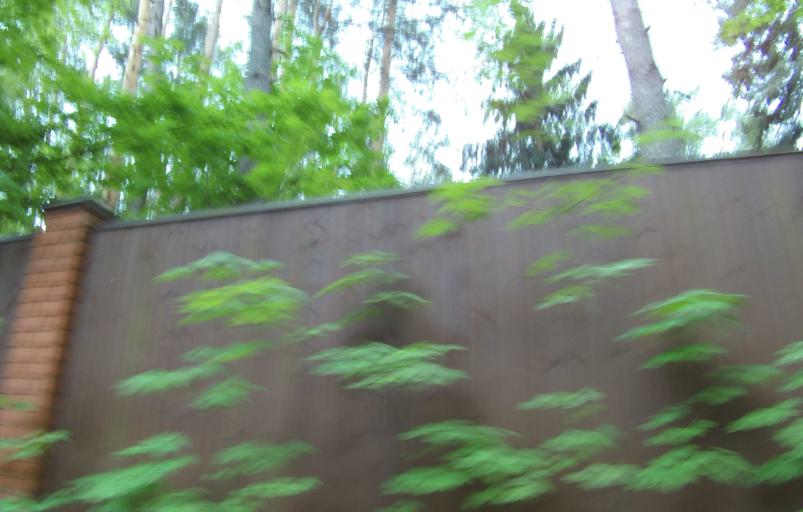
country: RU
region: Moskovskaya
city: Kratovo
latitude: 55.5820
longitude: 38.1669
